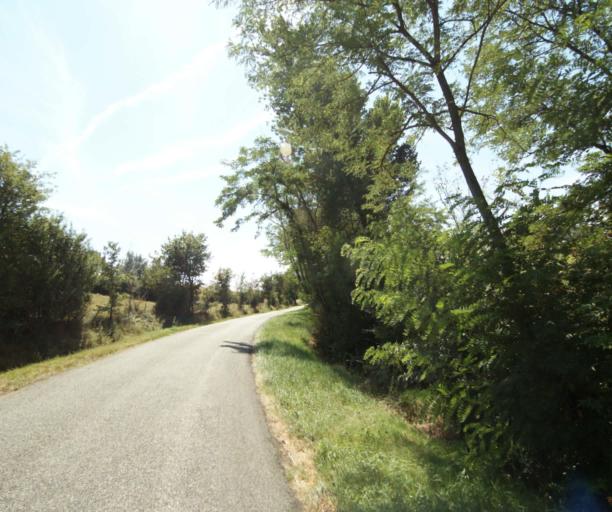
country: FR
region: Midi-Pyrenees
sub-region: Departement de l'Ariege
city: Lezat-sur-Leze
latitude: 43.2710
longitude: 1.3377
